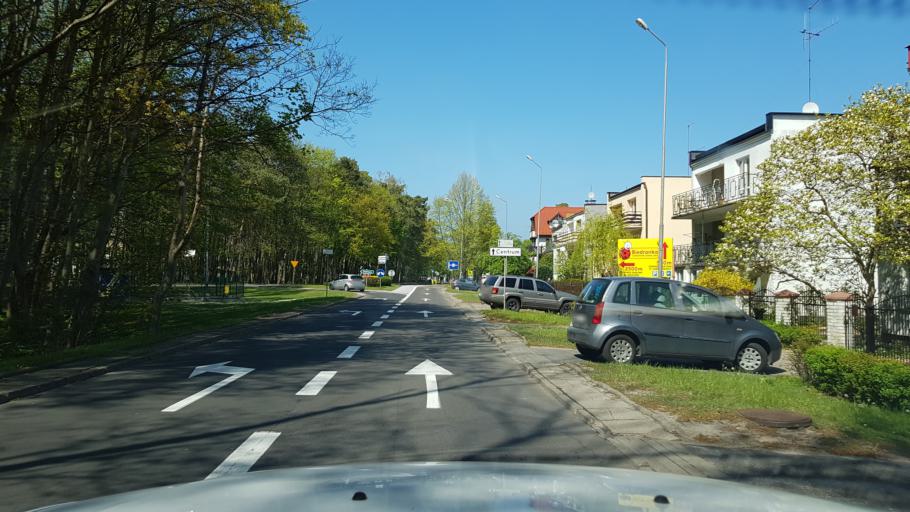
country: PL
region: Pomeranian Voivodeship
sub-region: Powiat slupski
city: Ustka
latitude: 54.5759
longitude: 16.8677
